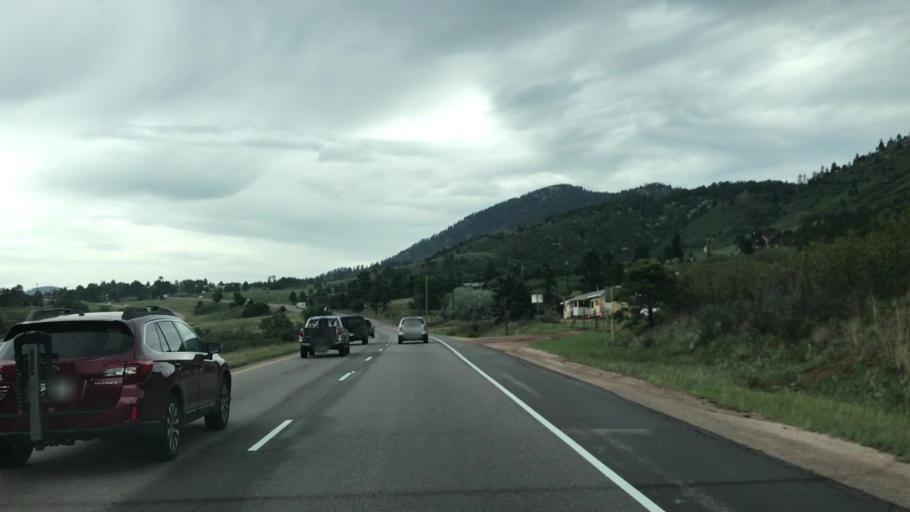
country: US
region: Colorado
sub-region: El Paso County
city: Cascade-Chipita Park
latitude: 38.9278
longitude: -104.9980
